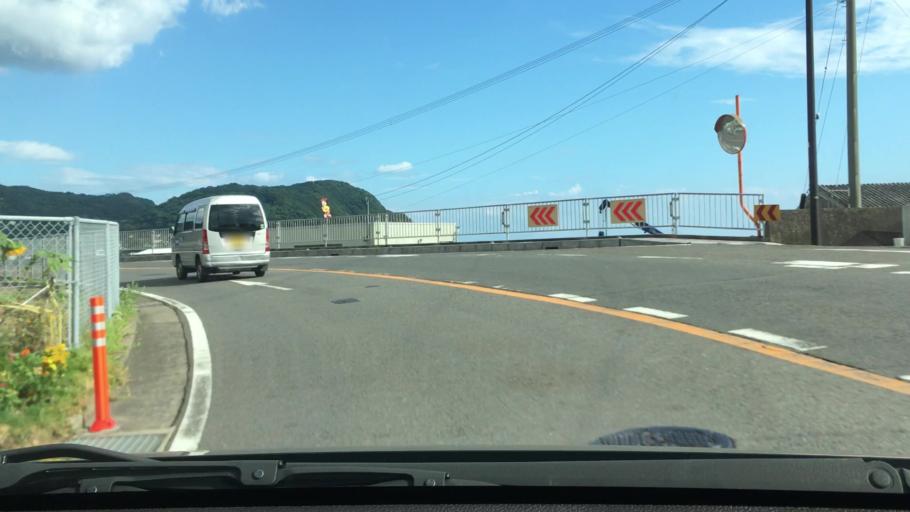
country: JP
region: Nagasaki
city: Togitsu
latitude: 32.8357
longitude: 129.7142
